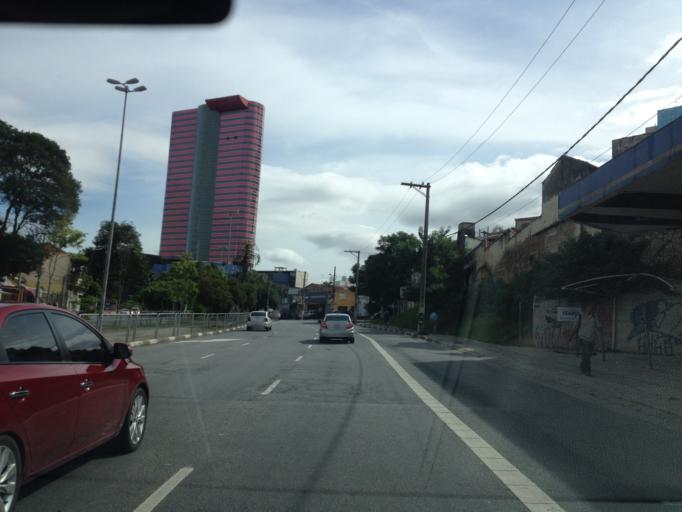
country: BR
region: Sao Paulo
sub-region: Sao Paulo
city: Sao Paulo
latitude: -23.5642
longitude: -46.6944
